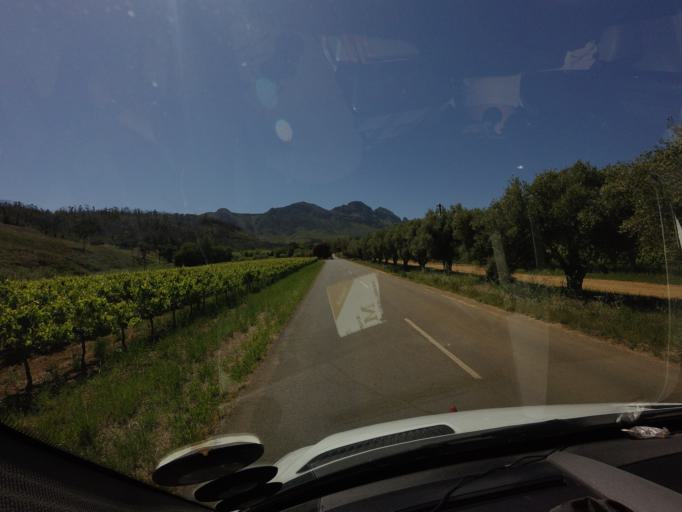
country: ZA
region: Western Cape
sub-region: Cape Winelands District Municipality
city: Stellenbosch
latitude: -33.8702
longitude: 18.8717
